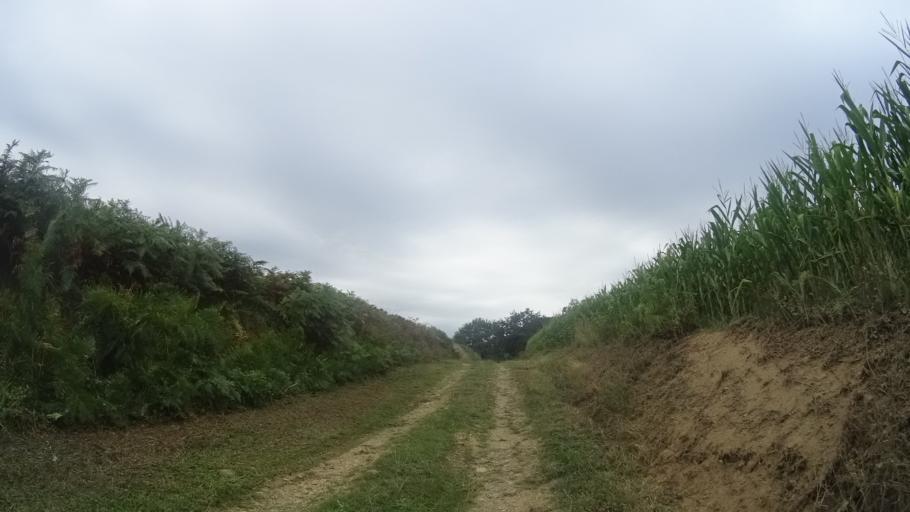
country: FR
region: Aquitaine
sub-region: Departement des Pyrenees-Atlantiques
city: Orthez
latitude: 43.4919
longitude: -0.7096
